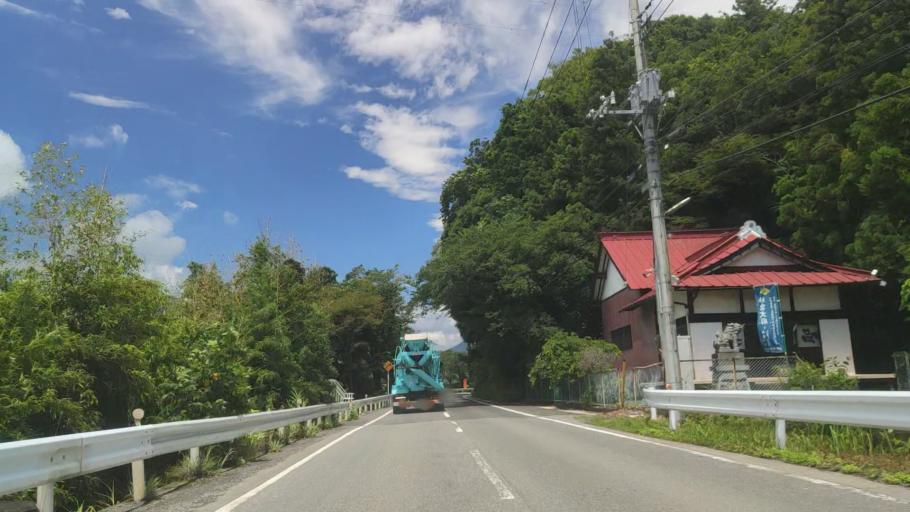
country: JP
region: Shizuoka
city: Fujinomiya
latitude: 35.3952
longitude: 138.4498
